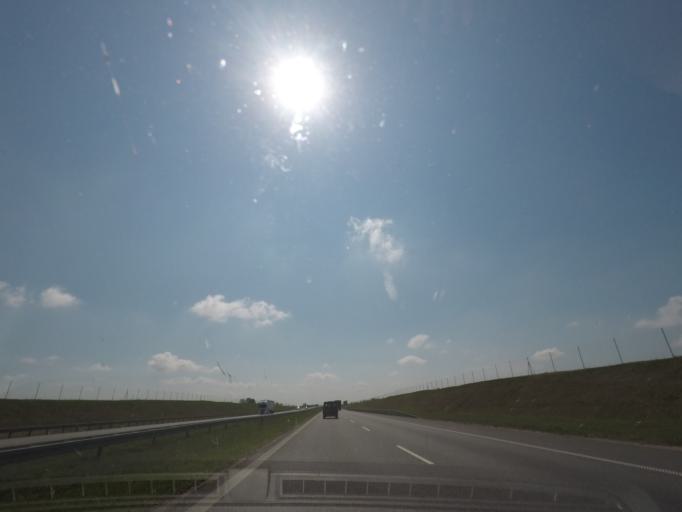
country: PL
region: Kujawsko-Pomorskie
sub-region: Powiat wloclawski
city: Czerniewice
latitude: 52.5518
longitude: 19.0404
